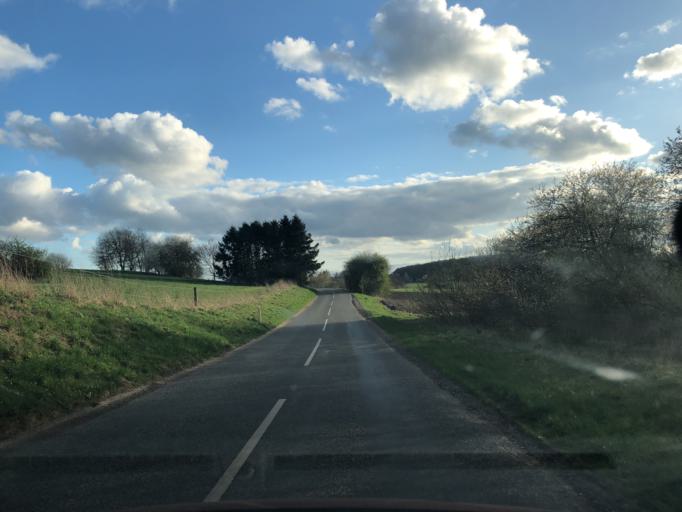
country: DK
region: Zealand
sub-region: Lejre Kommune
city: Kirke Hvalso
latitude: 55.5080
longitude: 11.8682
